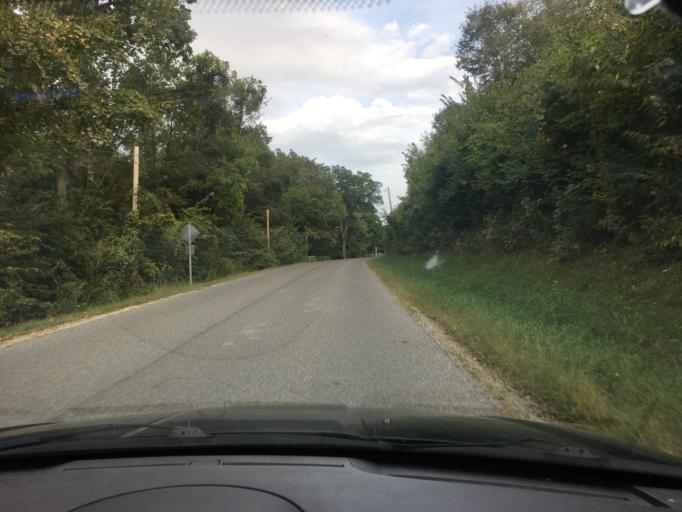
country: US
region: Ohio
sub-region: Logan County
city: West Liberty
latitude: 40.3020
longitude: -83.6975
